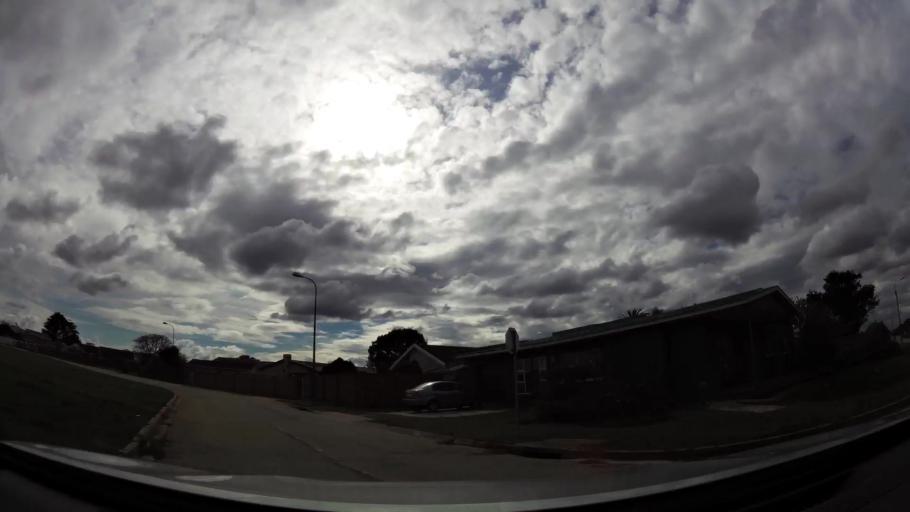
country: ZA
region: Eastern Cape
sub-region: Nelson Mandela Bay Metropolitan Municipality
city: Port Elizabeth
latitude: -33.9373
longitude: 25.5079
